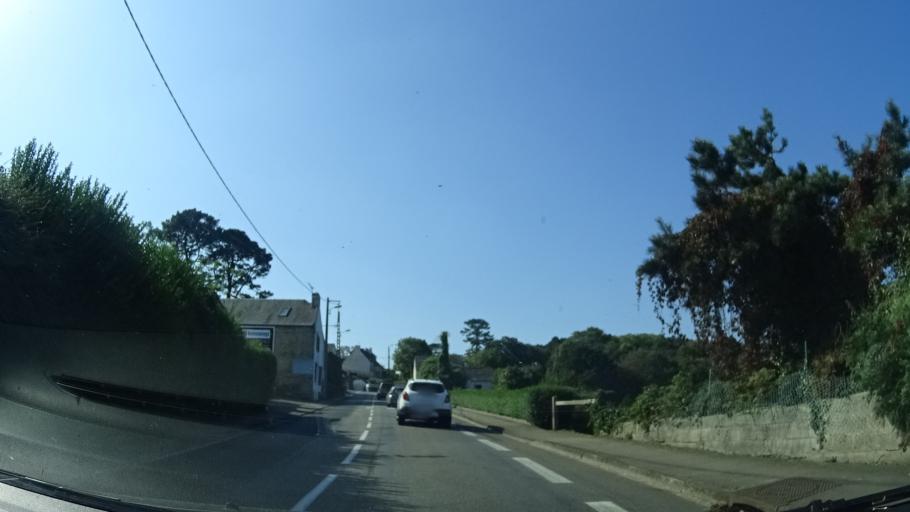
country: FR
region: Brittany
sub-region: Departement du Finistere
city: Douarnenez
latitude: 48.0890
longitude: -4.3037
